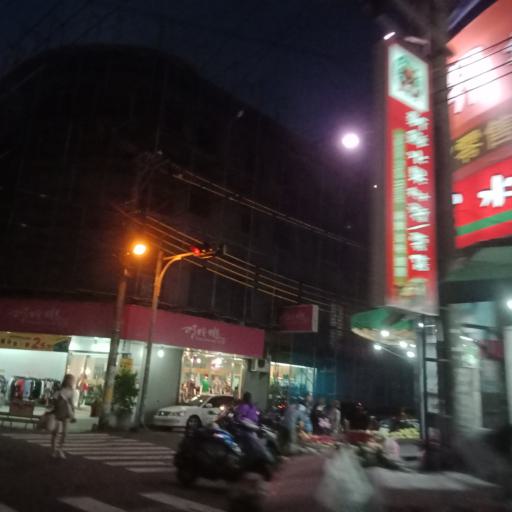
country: TW
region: Taiwan
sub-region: Hsinchu
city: Zhubei
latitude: 24.9023
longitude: 121.0482
